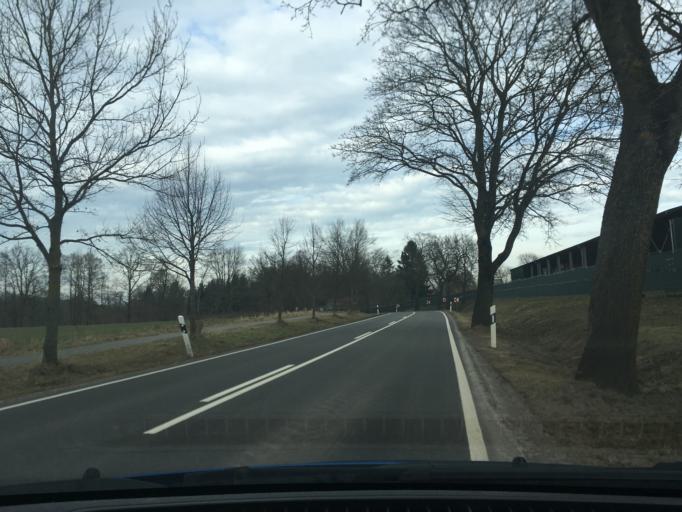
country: DE
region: Mecklenburg-Vorpommern
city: Boizenburg
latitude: 53.4231
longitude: 10.7467
